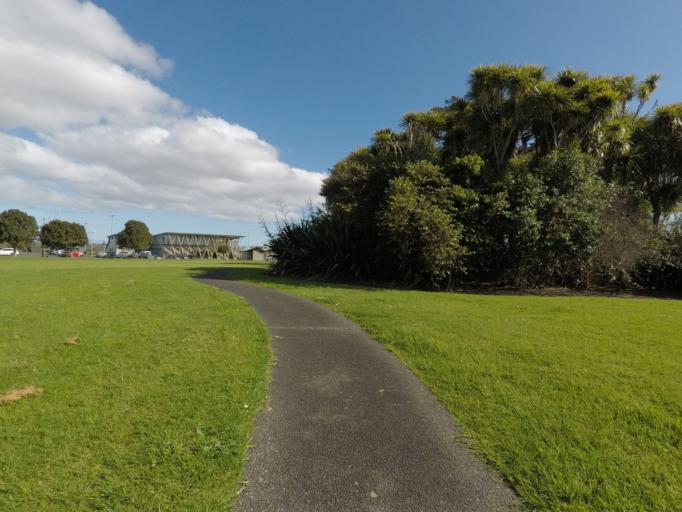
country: NZ
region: Auckland
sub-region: Auckland
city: Rosebank
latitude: -36.8584
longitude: 174.6046
